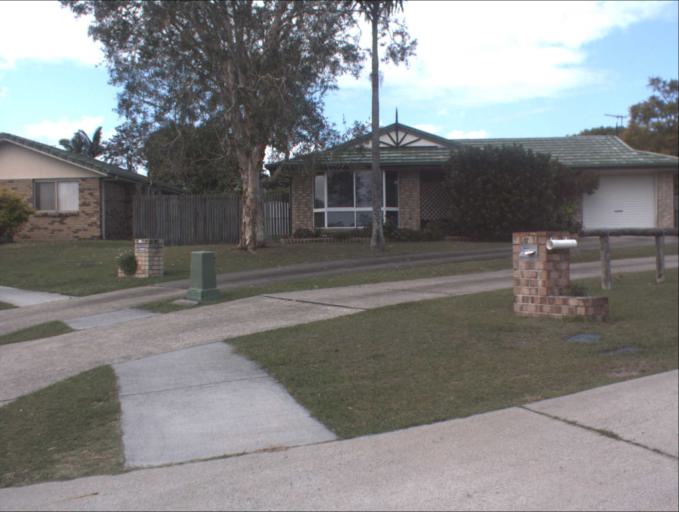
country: AU
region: Queensland
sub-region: Logan
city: Logan City
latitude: -27.6725
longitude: 153.0832
